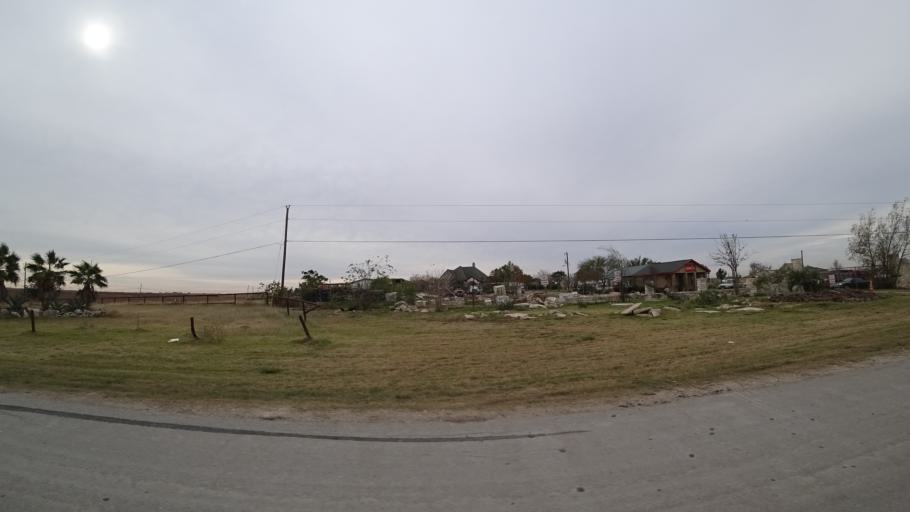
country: US
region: Texas
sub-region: Travis County
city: Garfield
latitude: 30.1032
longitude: -97.6145
